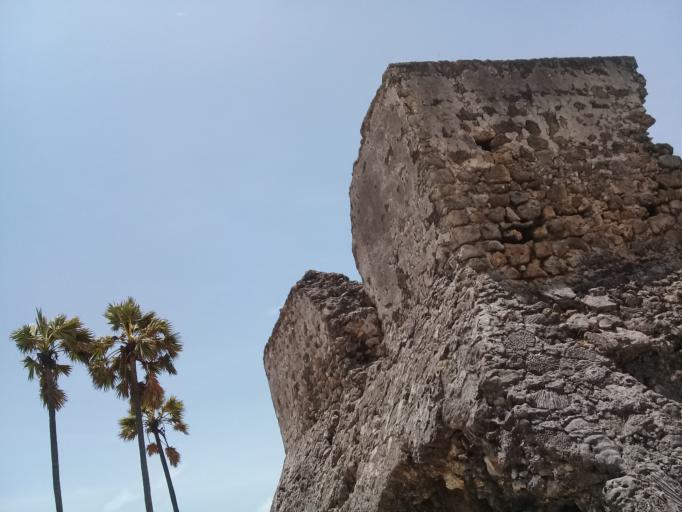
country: LK
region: Northern Province
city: Jaffna
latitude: 9.5276
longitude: 79.6997
